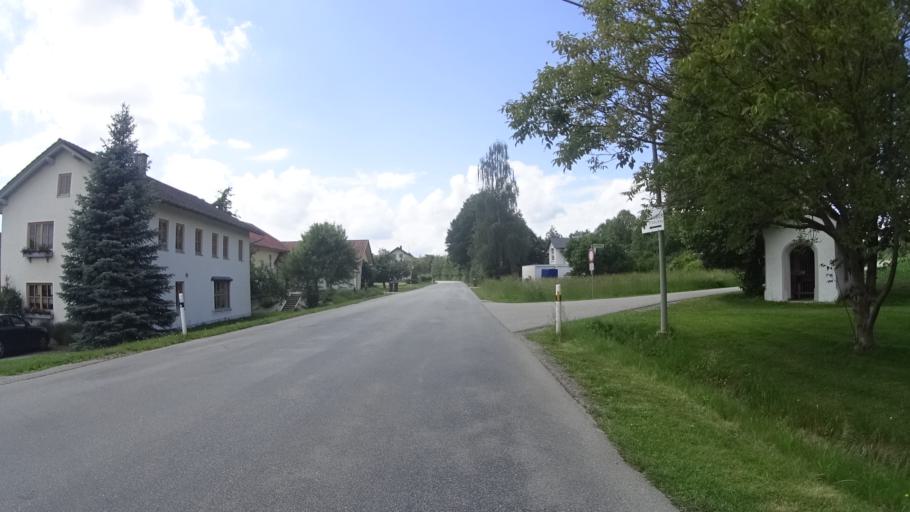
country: DE
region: Bavaria
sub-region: Lower Bavaria
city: Unterdietfurt
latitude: 48.3955
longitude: 12.6919
